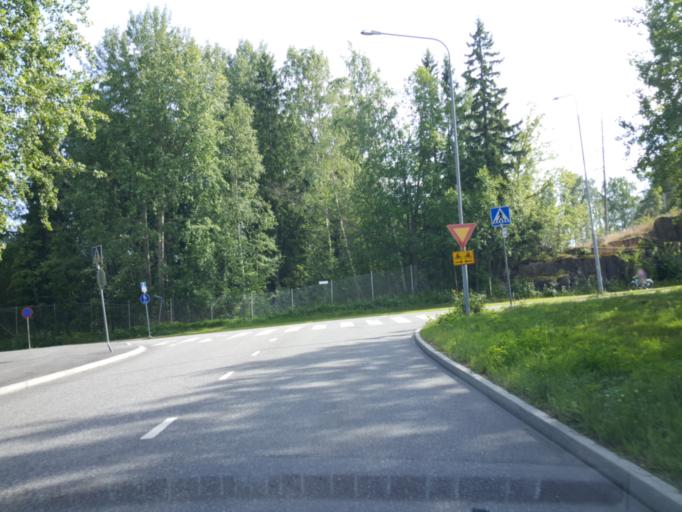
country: FI
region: Uusimaa
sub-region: Helsinki
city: Kilo
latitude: 60.2208
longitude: 24.7611
